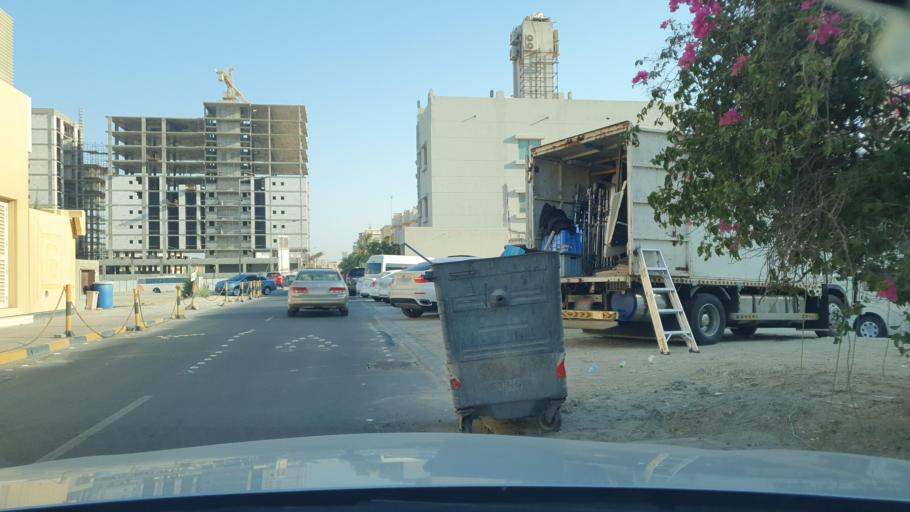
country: BH
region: Manama
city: Manama
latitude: 26.2193
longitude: 50.6141
